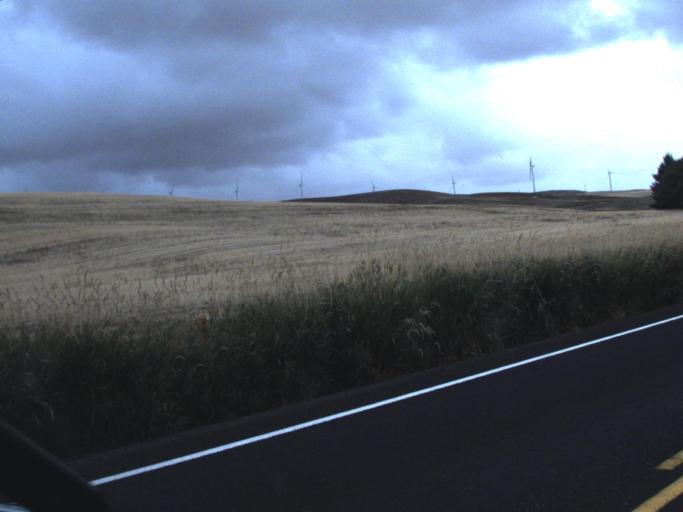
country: US
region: Washington
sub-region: Whitman County
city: Colfax
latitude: 47.1864
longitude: -117.3246
